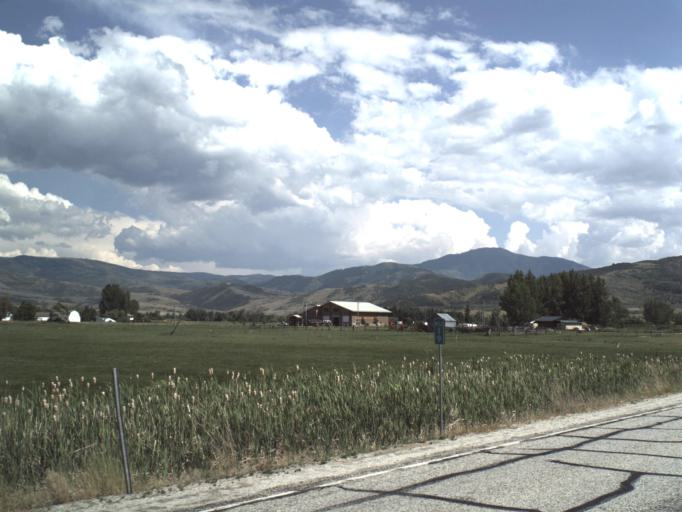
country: US
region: Utah
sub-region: Weber County
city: Wolf Creek
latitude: 41.2603
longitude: -111.7615
